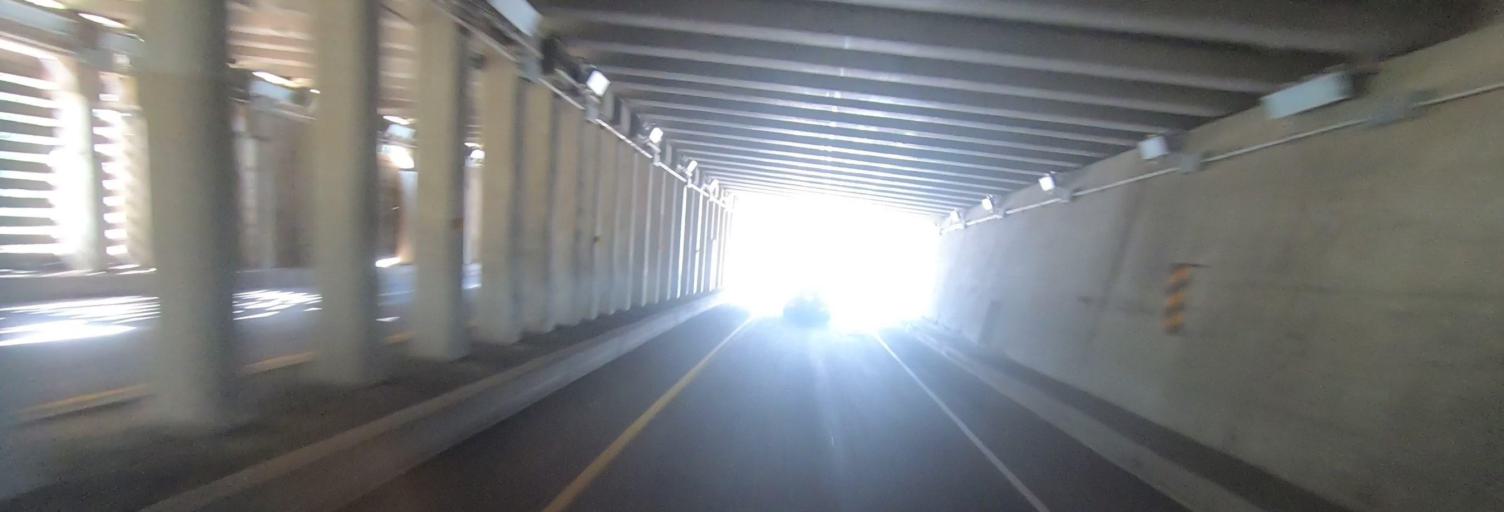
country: CA
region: British Columbia
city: Golden
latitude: 51.3233
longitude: -117.4818
